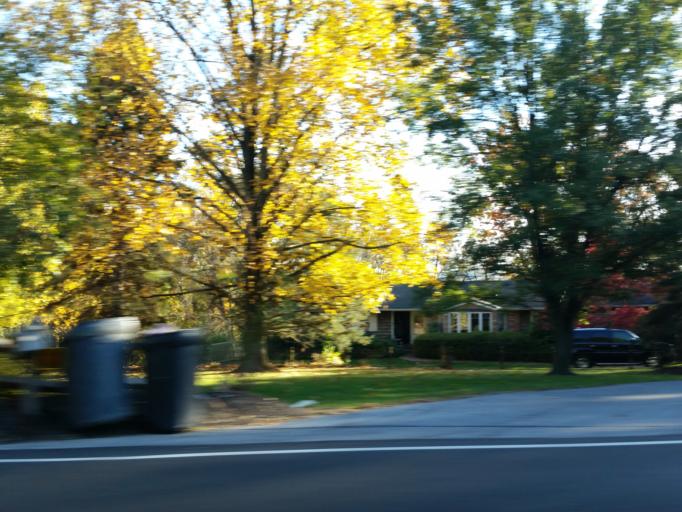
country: US
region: Pennsylvania
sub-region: Lebanon County
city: Cleona
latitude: 40.3448
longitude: -76.4823
